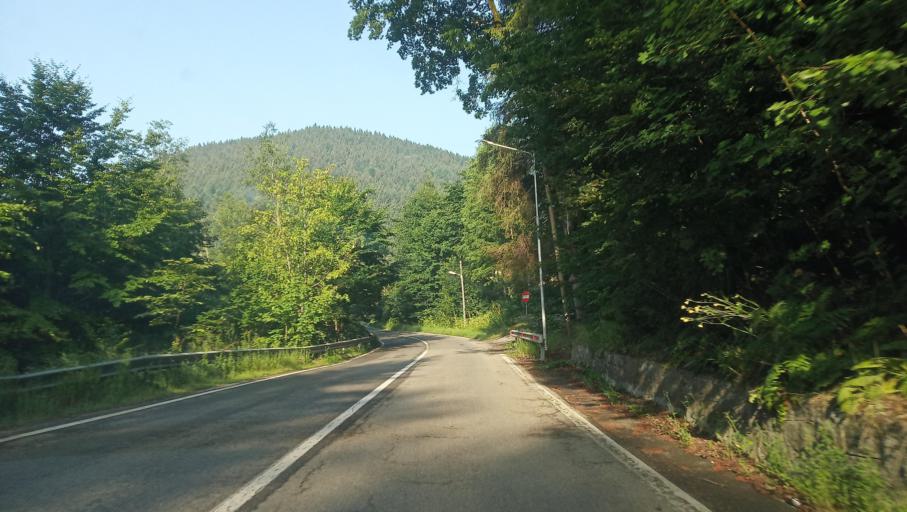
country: RO
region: Prahova
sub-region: Oras Sinaia
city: Sinaia
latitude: 45.3253
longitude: 25.5337
